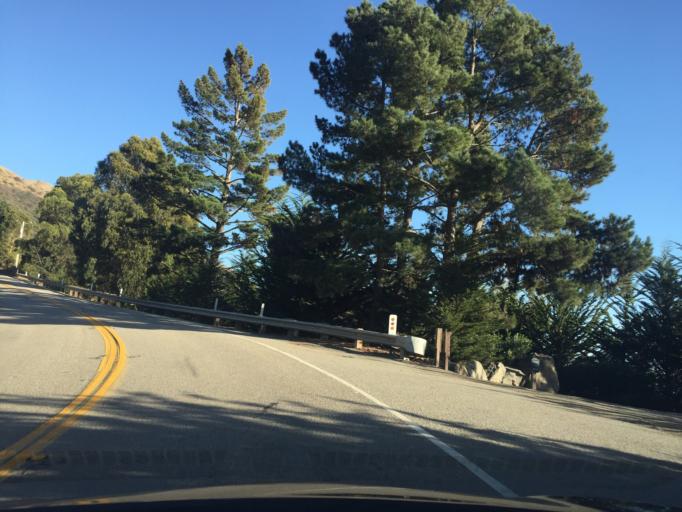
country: US
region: California
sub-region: San Luis Obispo County
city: Cambria
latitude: 35.8063
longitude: -121.3565
